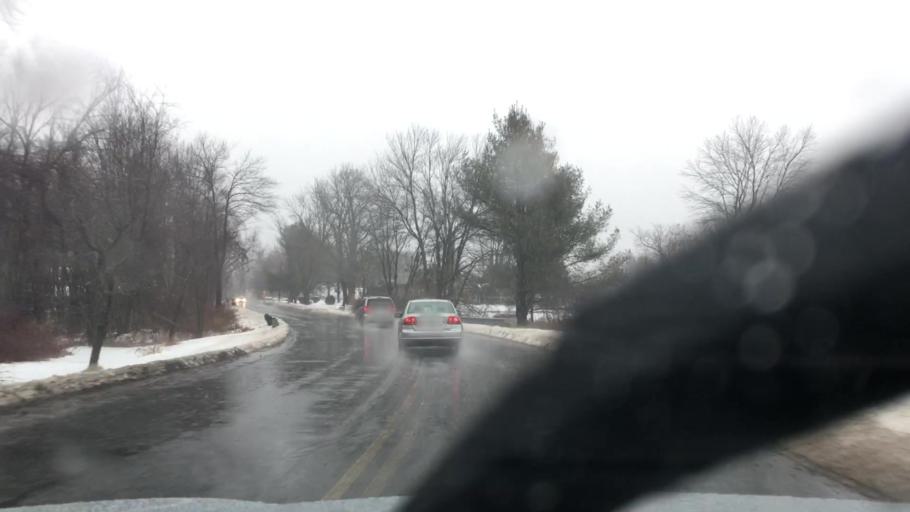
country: US
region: Massachusetts
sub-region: Hampshire County
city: Granby
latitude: 42.2223
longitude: -72.4976
